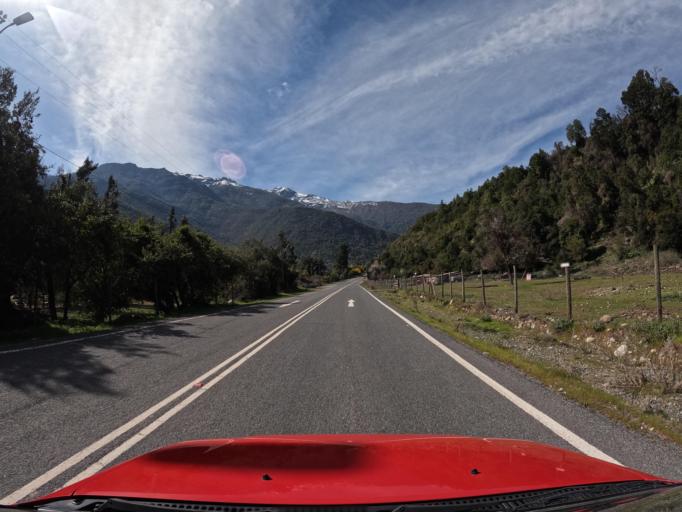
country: CL
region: O'Higgins
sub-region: Provincia de Colchagua
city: Chimbarongo
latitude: -35.0005
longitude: -70.8230
